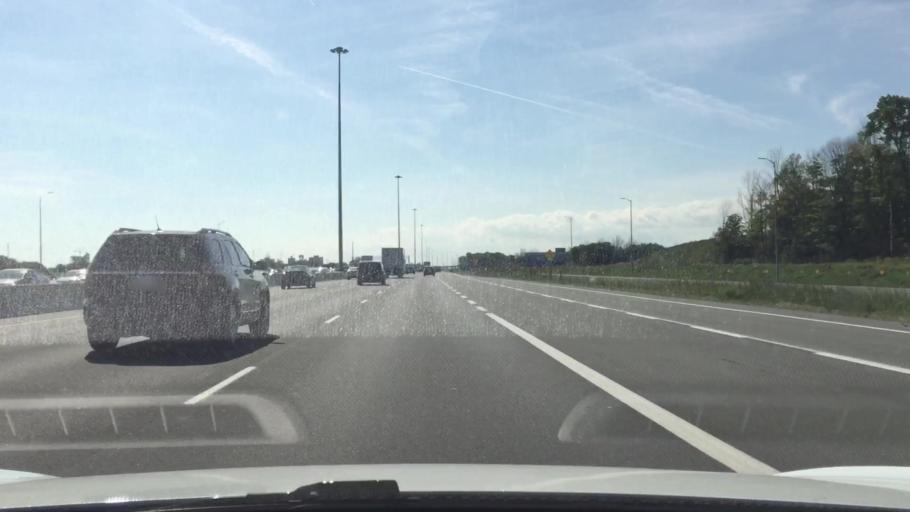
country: CA
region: Ontario
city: Ajax
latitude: 43.8615
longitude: -78.9876
